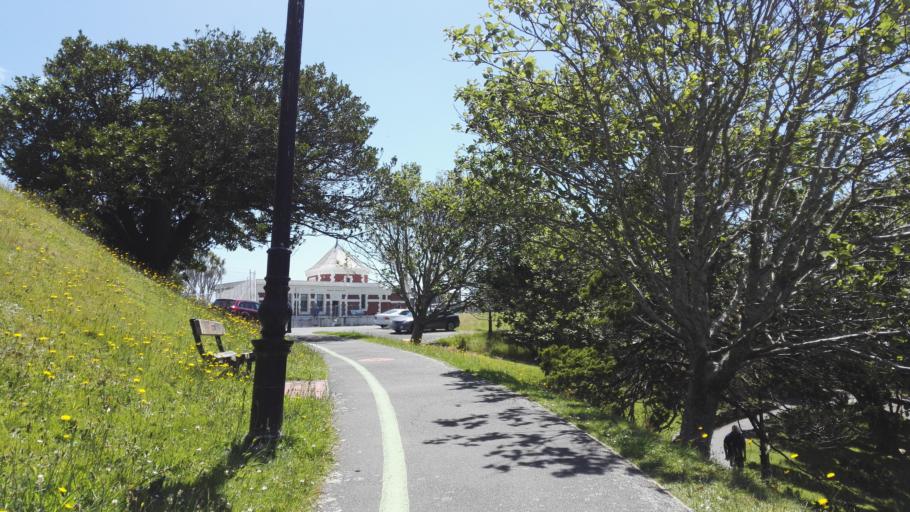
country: NZ
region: Wellington
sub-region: Wellington City
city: Kelburn
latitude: -41.2849
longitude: 174.7678
